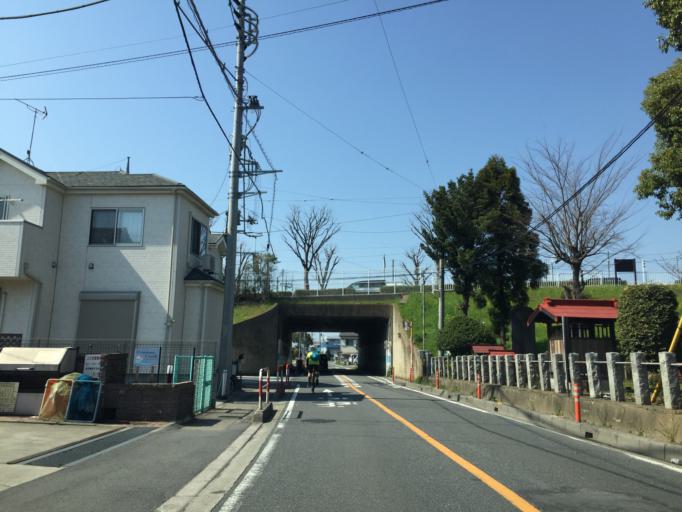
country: JP
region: Saitama
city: Shiki
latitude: 35.8515
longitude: 139.5847
